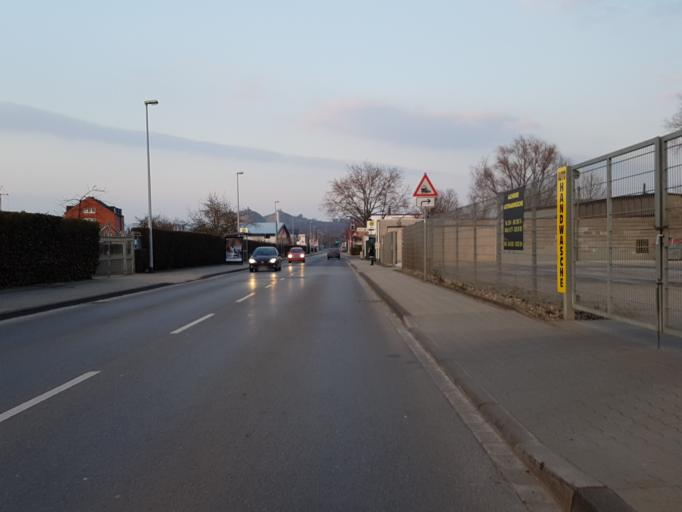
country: DE
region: North Rhine-Westphalia
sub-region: Regierungsbezirk Koln
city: Aachen
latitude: 50.7913
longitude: 6.1075
